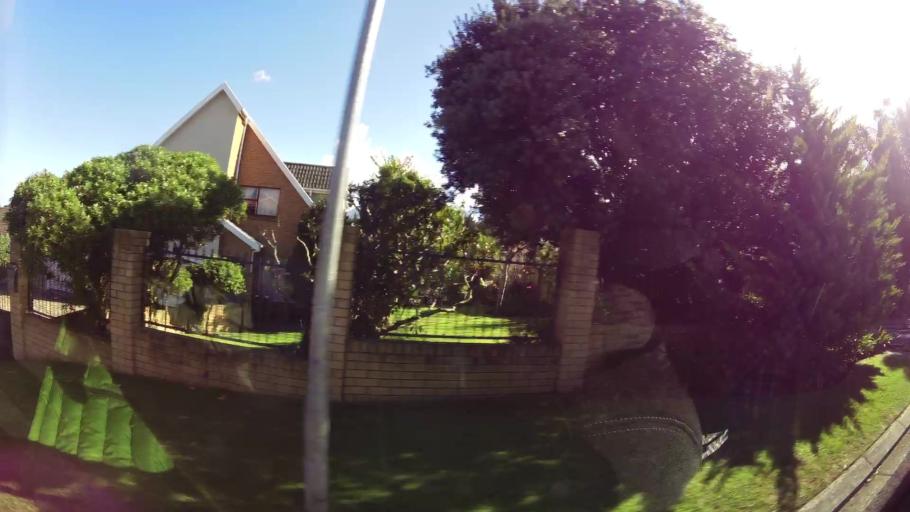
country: ZA
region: Western Cape
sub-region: Eden District Municipality
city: George
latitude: -33.9464
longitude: 22.4618
